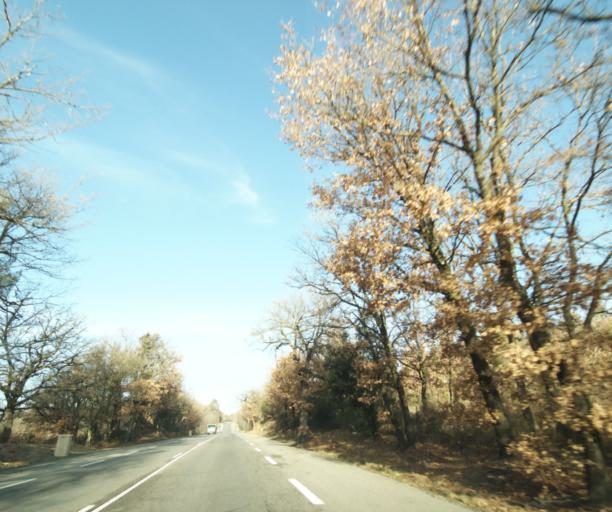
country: FR
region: Provence-Alpes-Cote d'Azur
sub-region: Departement du Var
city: Saint-Maximin-la-Sainte-Baume
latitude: 43.4319
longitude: 5.8837
